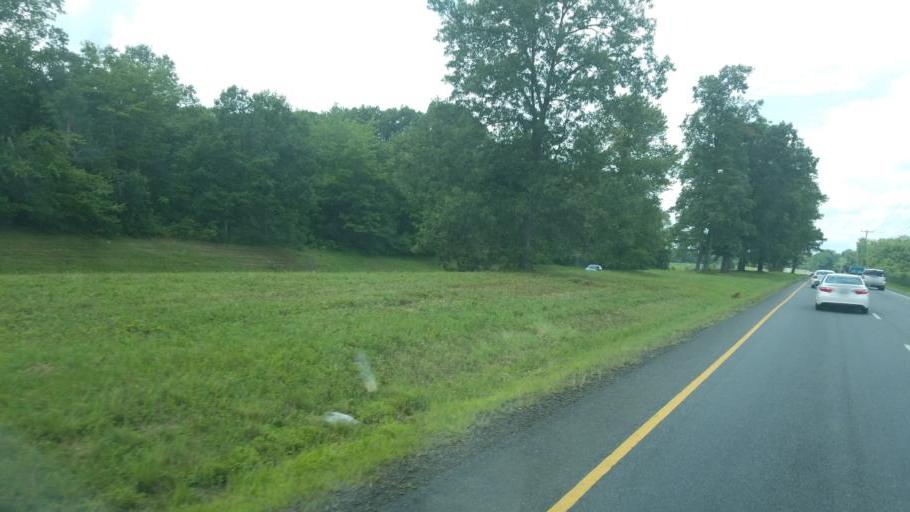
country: US
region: Virginia
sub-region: Fauquier County
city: Marshall
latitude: 38.8485
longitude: -77.8313
